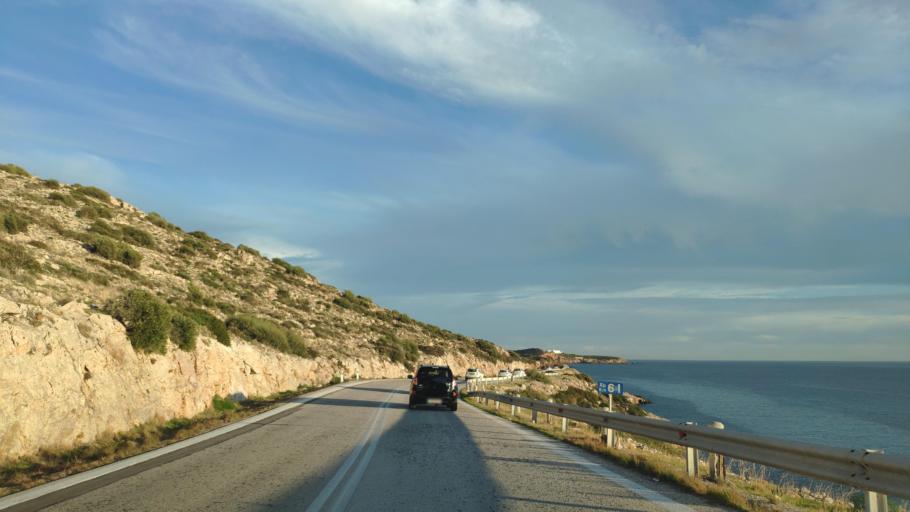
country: GR
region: Attica
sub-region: Nomarchia Anatolikis Attikis
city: Palaia Fokaia
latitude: 37.6672
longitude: 23.9602
